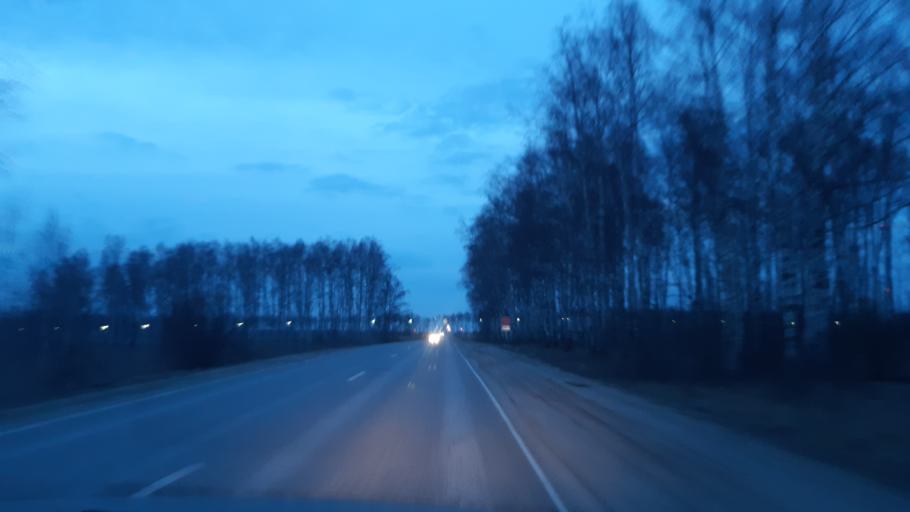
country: RU
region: Vladimir
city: Luknovo
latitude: 56.2333
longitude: 42.0344
